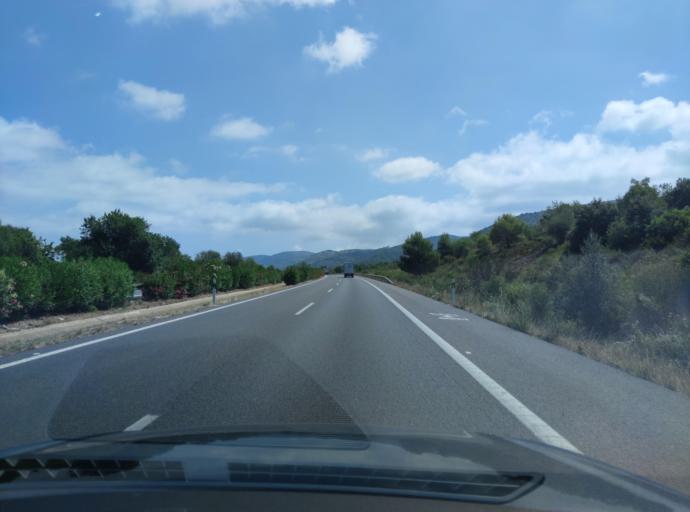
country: ES
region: Valencia
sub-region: Provincia de Castello
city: Santa Magdalena de Pulpis
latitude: 40.3462
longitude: 0.2862
